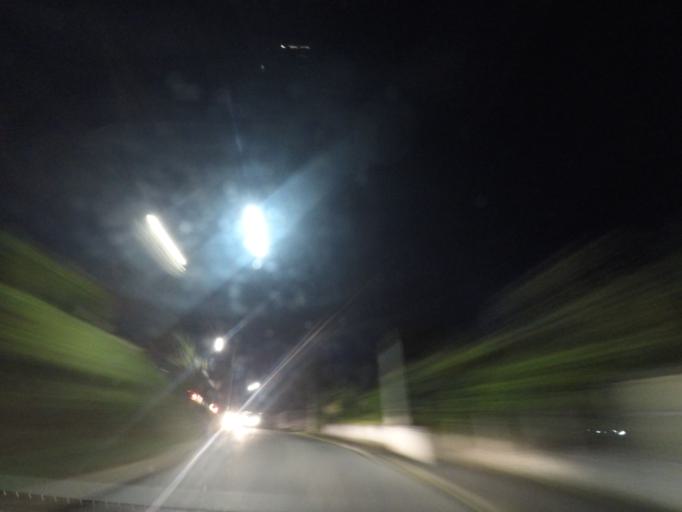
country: BR
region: Parana
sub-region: Curitiba
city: Curitiba
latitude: -25.4115
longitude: -49.3227
